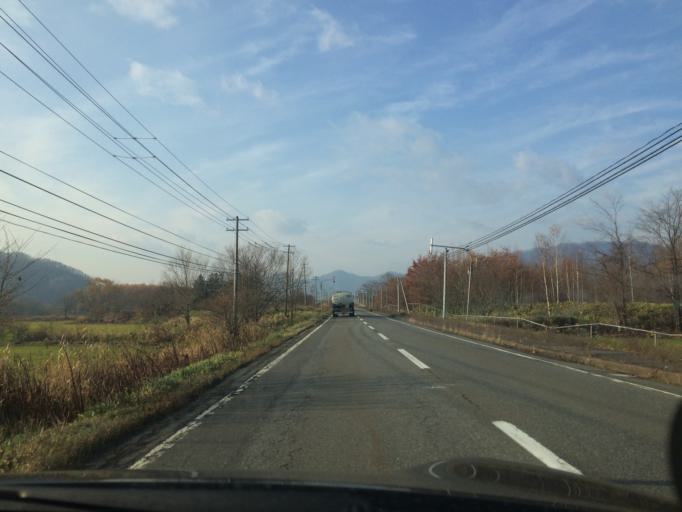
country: JP
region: Hokkaido
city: Shimo-furano
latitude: 42.8896
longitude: 142.4662
